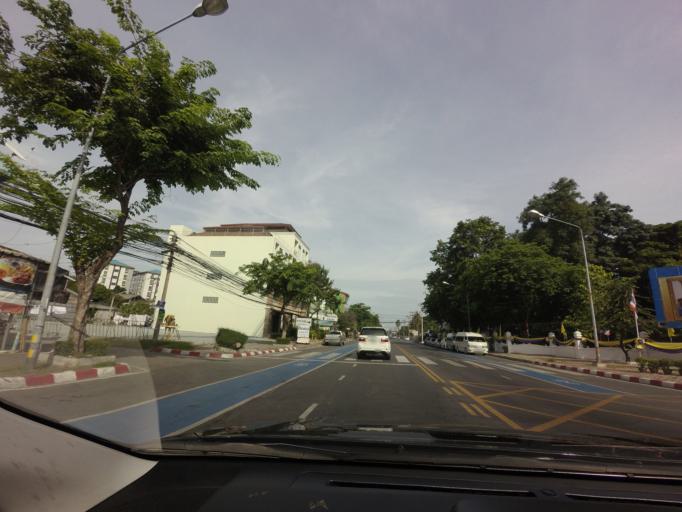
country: TH
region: Chon Buri
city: Chon Buri
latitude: 13.2885
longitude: 100.9149
